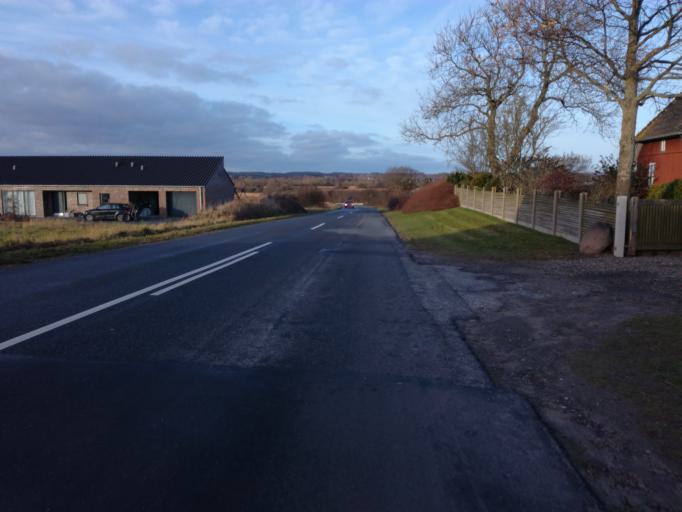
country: DK
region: South Denmark
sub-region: Fredericia Kommune
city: Fredericia
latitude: 55.6179
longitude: 9.7439
